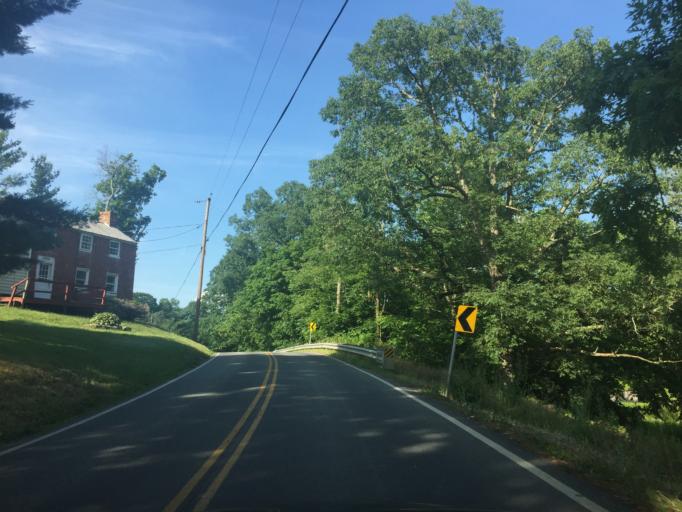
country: US
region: Maryland
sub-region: Harford County
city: Jarrettsville
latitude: 39.6548
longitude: -76.4888
